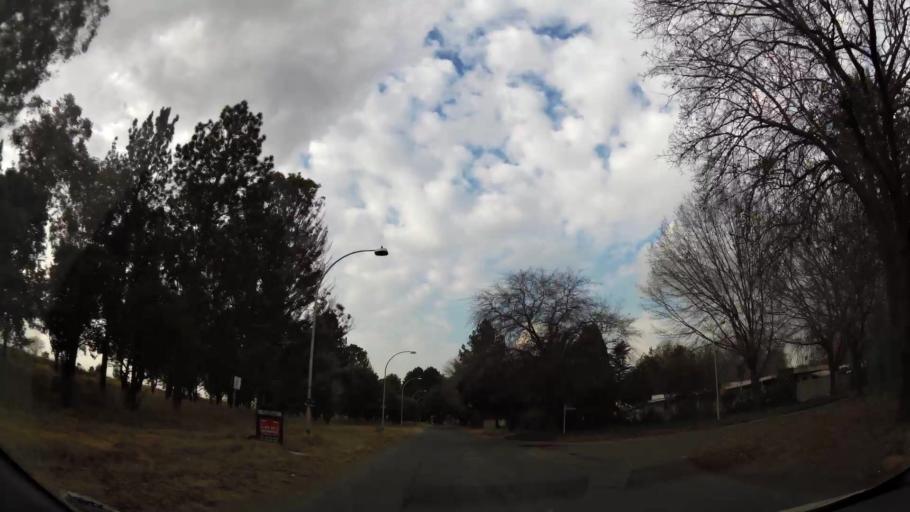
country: ZA
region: Orange Free State
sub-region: Fezile Dabi District Municipality
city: Sasolburg
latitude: -26.7903
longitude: 27.8181
